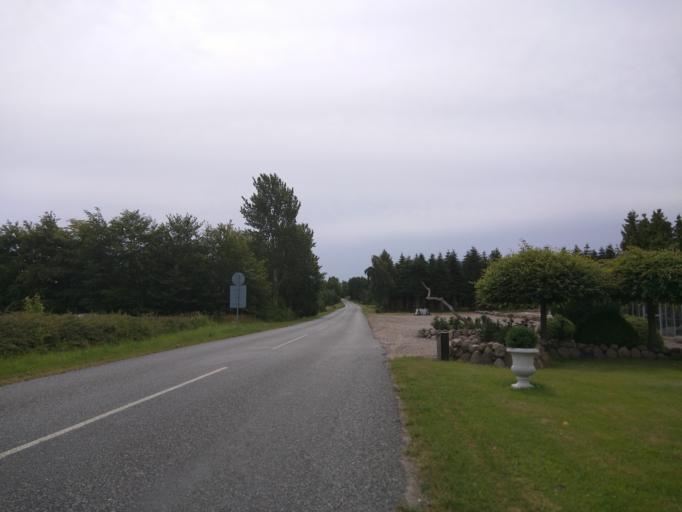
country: DK
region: Zealand
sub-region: Kalundborg Kommune
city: Svebolle
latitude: 55.6819
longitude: 11.3185
